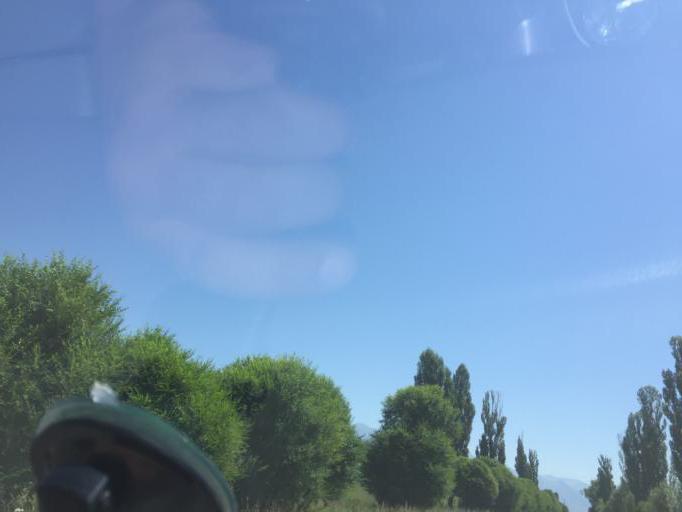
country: KG
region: Ysyk-Koel
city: Tyup
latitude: 42.7450
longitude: 78.4189
